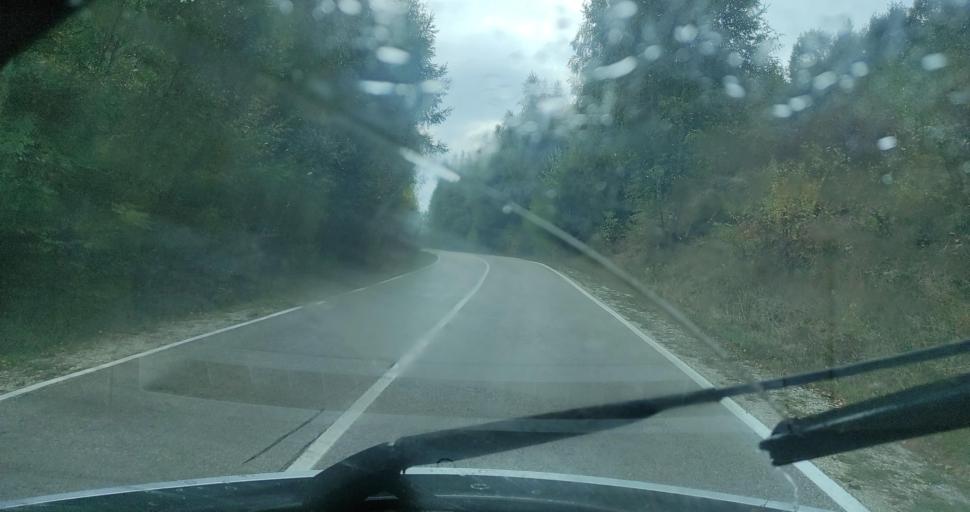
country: RS
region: Central Serbia
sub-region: Jablanicki Okrug
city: Crna Trava
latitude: 42.7153
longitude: 22.3291
